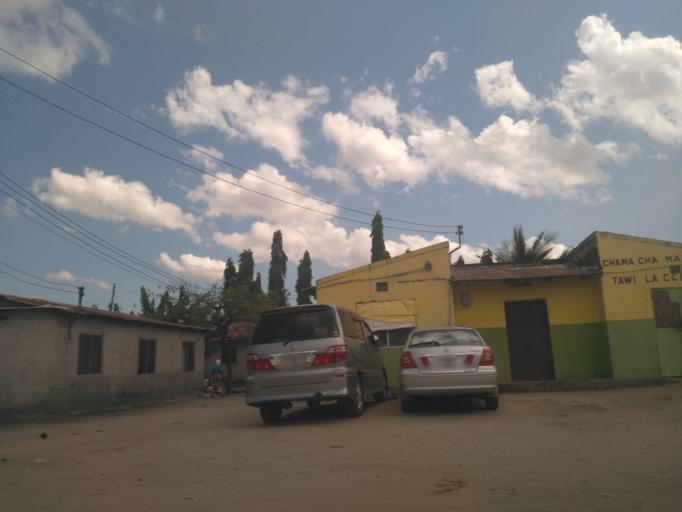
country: TZ
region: Dar es Salaam
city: Dar es Salaam
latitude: -6.8715
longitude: 39.2343
